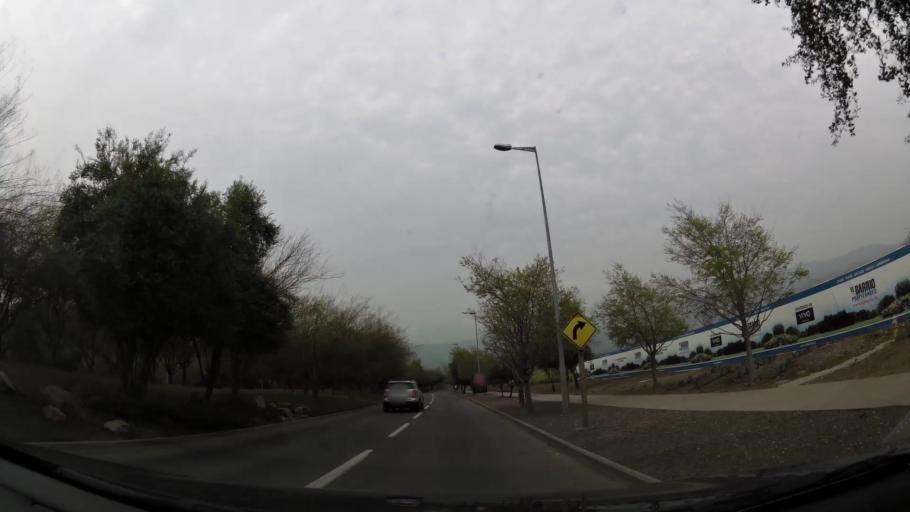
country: CL
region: Santiago Metropolitan
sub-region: Provincia de Chacabuco
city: Chicureo Abajo
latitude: -33.2803
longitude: -70.6341
